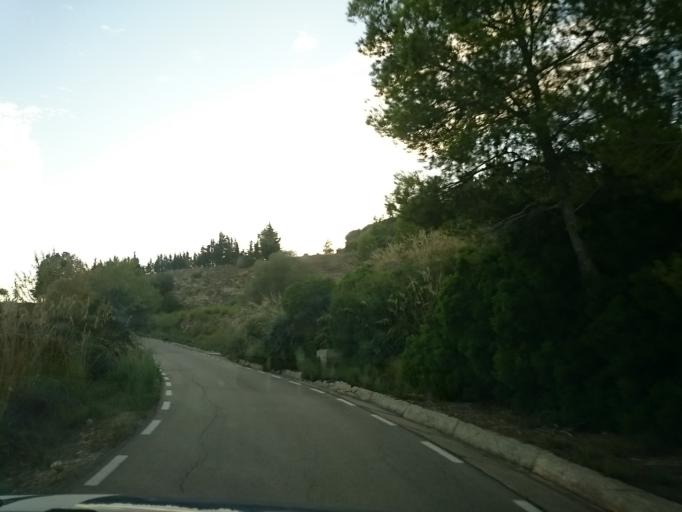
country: ES
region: Catalonia
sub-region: Provincia de Barcelona
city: Olivella
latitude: 41.3073
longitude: 1.8397
